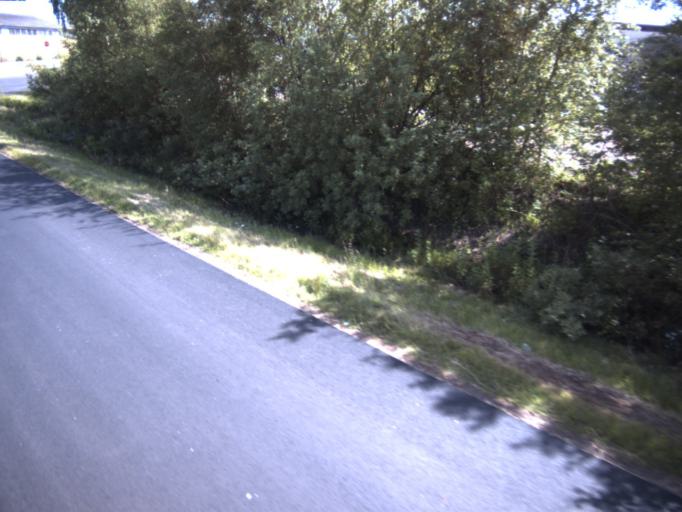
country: SE
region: Skane
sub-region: Helsingborg
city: Odakra
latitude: 56.0668
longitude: 12.7569
